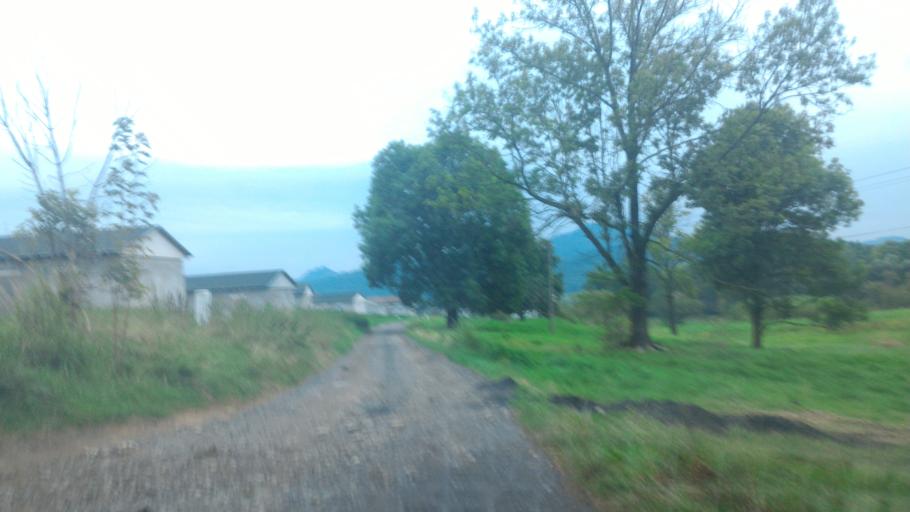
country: CZ
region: Ustecky
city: Dolni Podluzi
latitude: 50.8917
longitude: 14.5571
